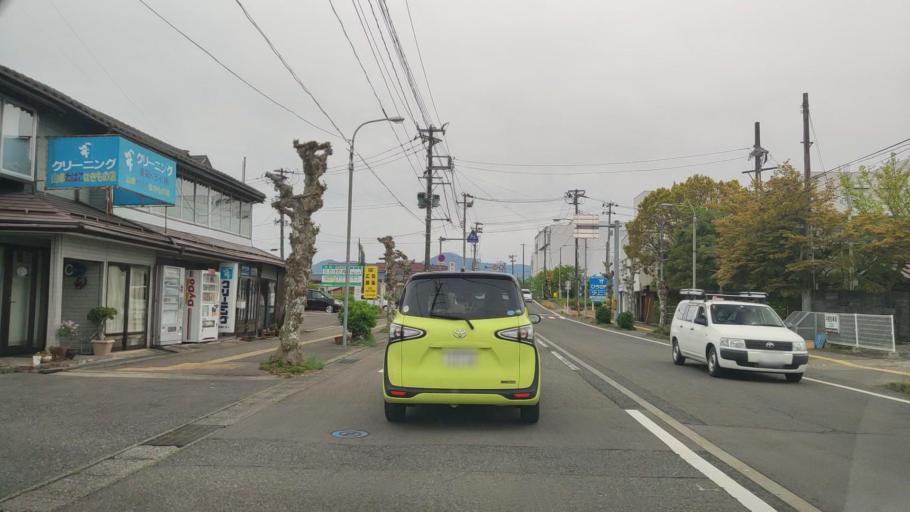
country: JP
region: Niigata
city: Gosen
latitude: 37.7363
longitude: 139.1765
